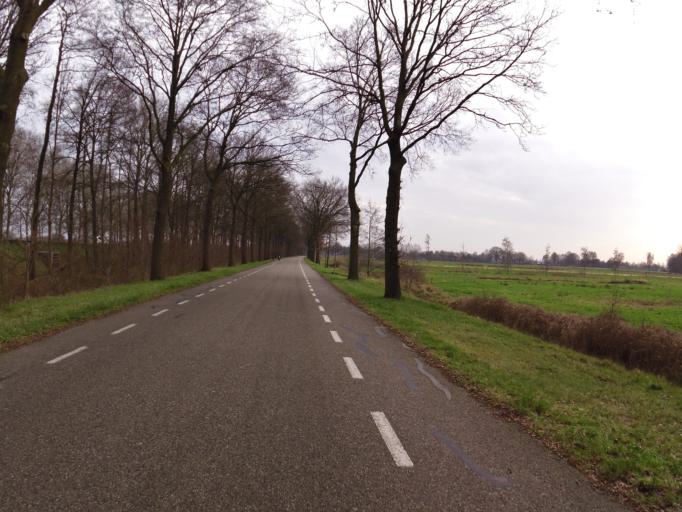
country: NL
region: North Brabant
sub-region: Gemeente Sint-Michielsgestel
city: Sint-Michielsgestel
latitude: 51.6664
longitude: 5.3363
